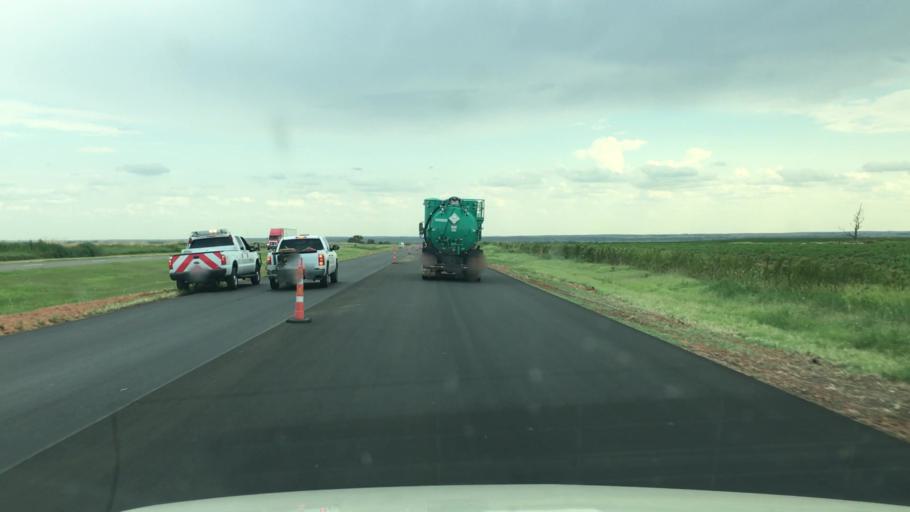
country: US
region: Texas
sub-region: Hall County
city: Memphis
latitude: 34.6159
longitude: -100.4707
